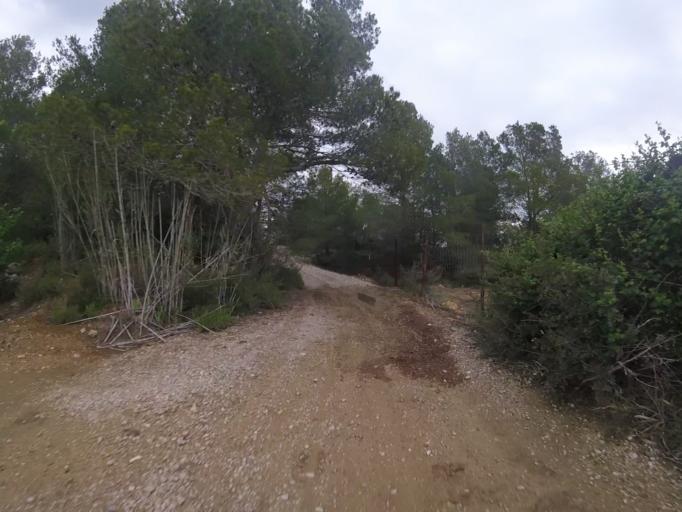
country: ES
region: Valencia
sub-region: Provincia de Castello
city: Cuevas de Vinroma
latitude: 40.2582
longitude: 0.0792
